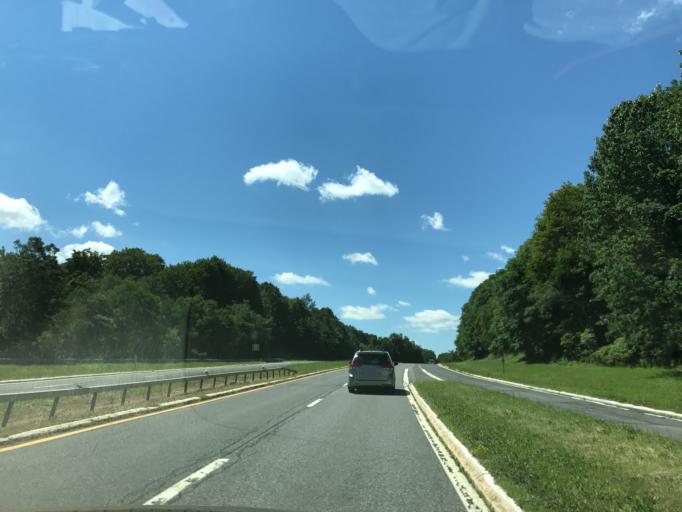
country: US
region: New York
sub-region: Dutchess County
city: Pine Plains
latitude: 41.9109
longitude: -73.7680
